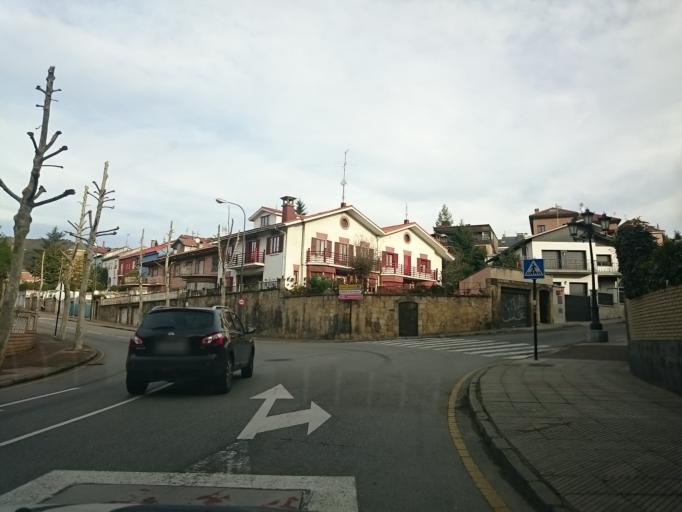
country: ES
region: Asturias
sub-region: Province of Asturias
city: Oviedo
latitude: 43.3636
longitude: -5.8578
